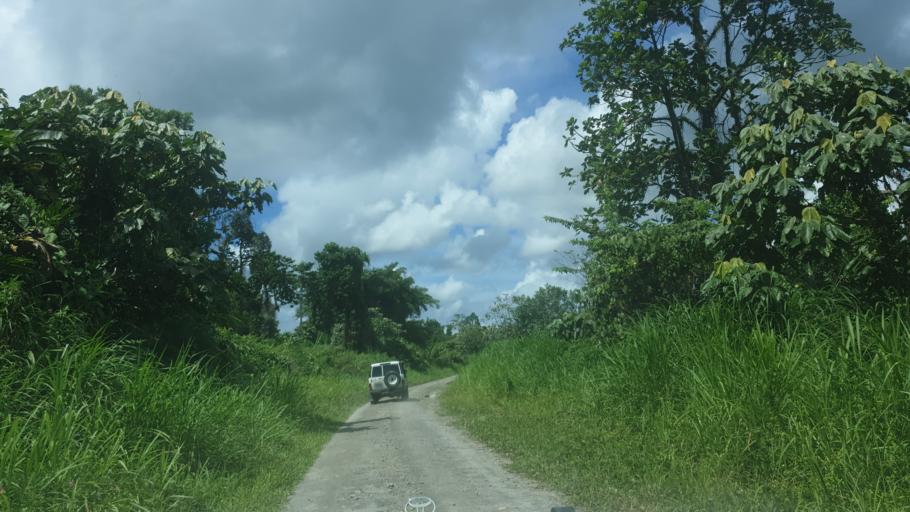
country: PG
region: Bougainville
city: Panguna
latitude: -6.7366
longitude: 155.5003
